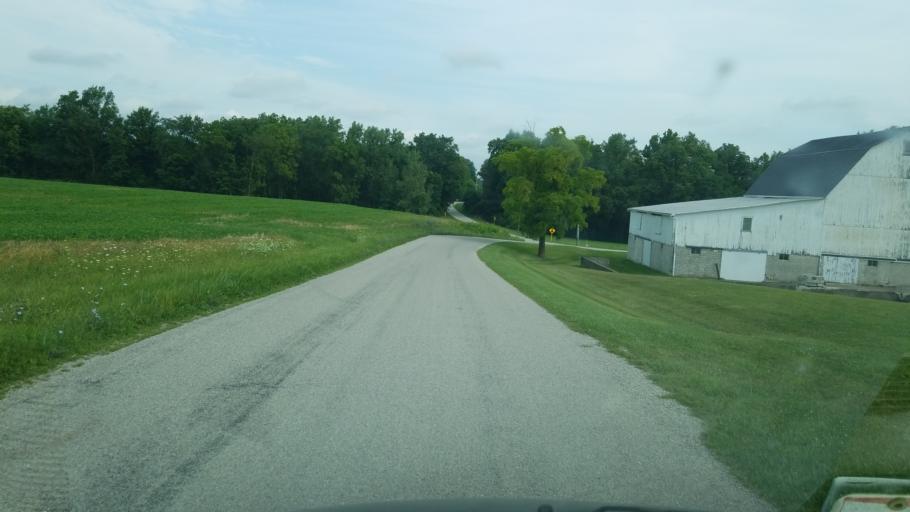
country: US
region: Ohio
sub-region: Seneca County
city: Tiffin
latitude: 41.1505
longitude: -83.0945
